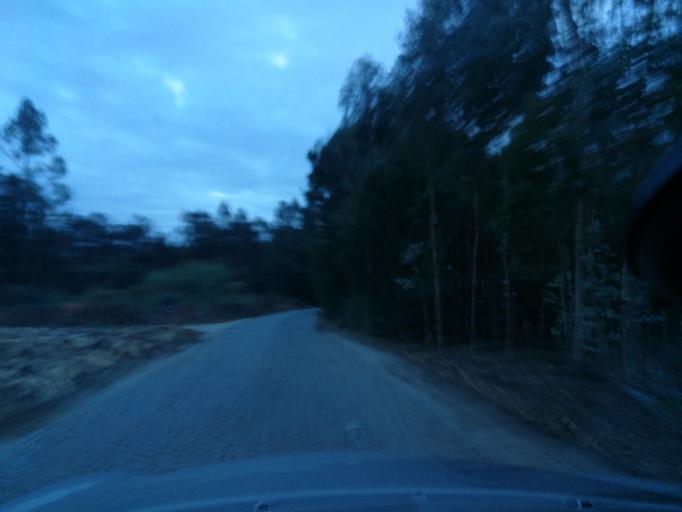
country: PT
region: Aveiro
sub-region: Estarreja
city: Estarreja
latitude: 40.7617
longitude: -8.6017
